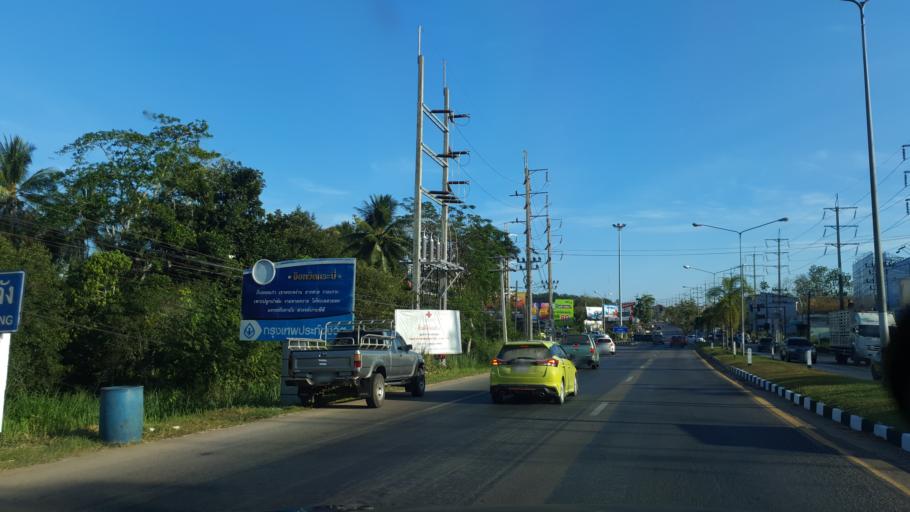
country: TH
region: Krabi
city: Krabi
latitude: 8.1019
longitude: 98.8838
